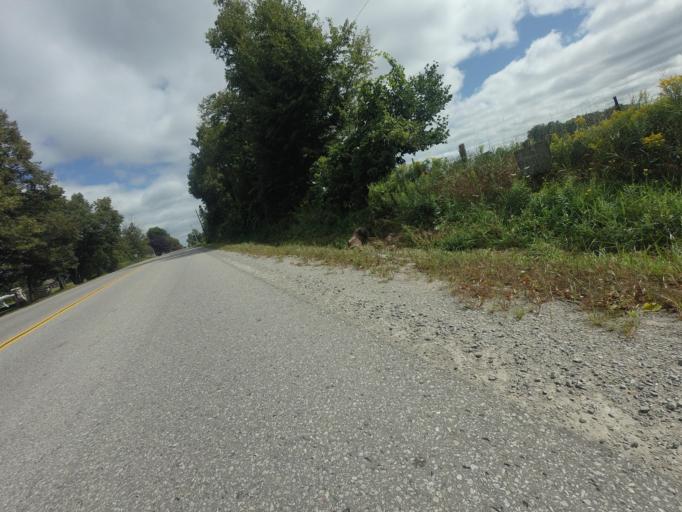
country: CA
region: Ontario
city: Uxbridge
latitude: 44.1275
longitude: -79.1574
